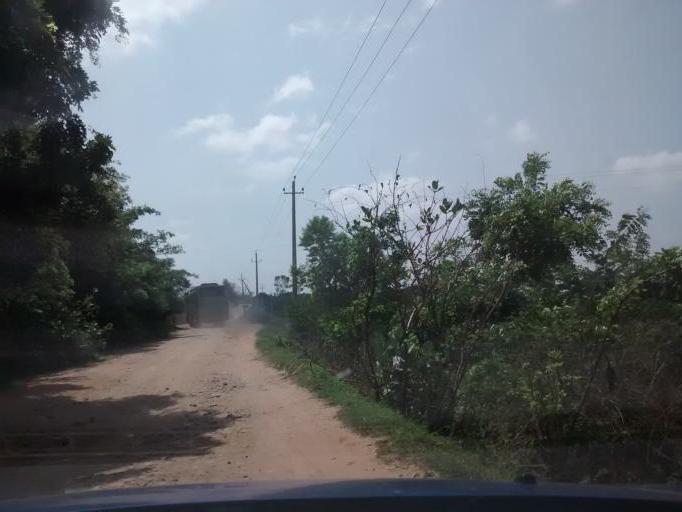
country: IN
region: Karnataka
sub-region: Hassan
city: Hole Narsipur
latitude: 12.6970
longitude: 76.1724
